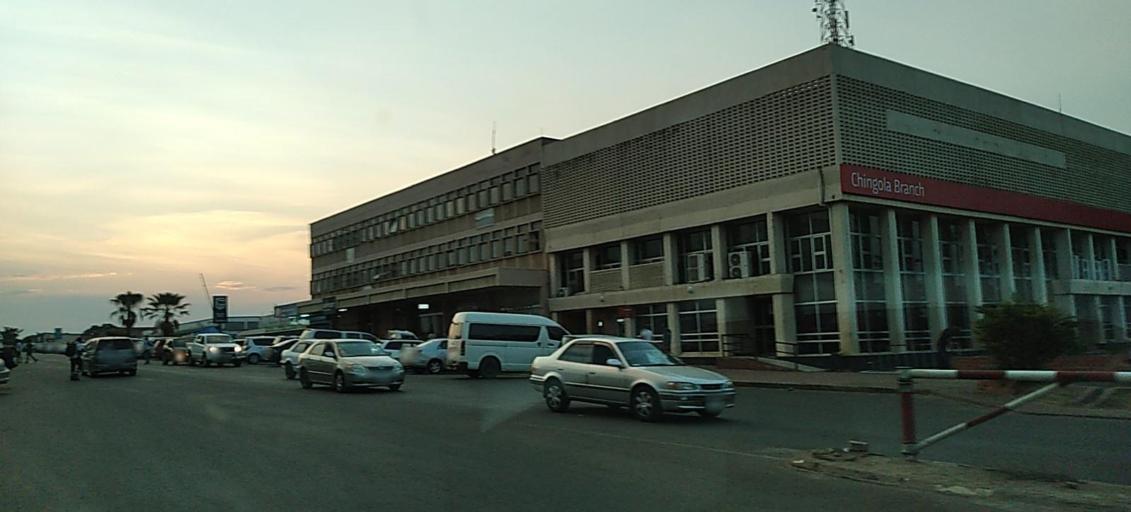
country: ZM
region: Copperbelt
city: Chingola
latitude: -12.5436
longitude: 27.8659
